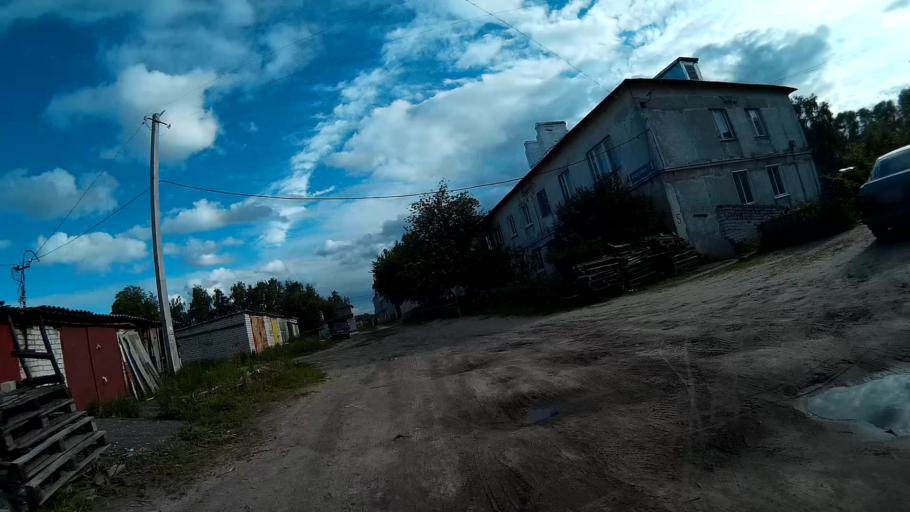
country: RU
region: Ulyanovsk
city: Novoul'yanovsk
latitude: 54.2057
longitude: 48.2653
